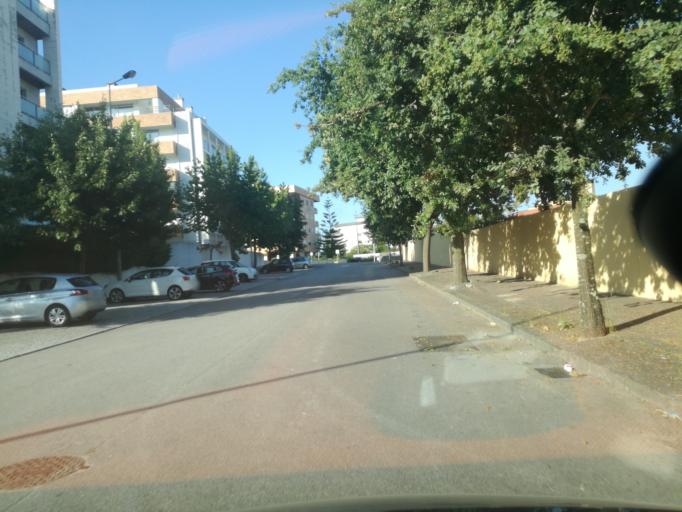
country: PT
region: Porto
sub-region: Maia
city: Anta
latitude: 41.2631
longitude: -8.6232
